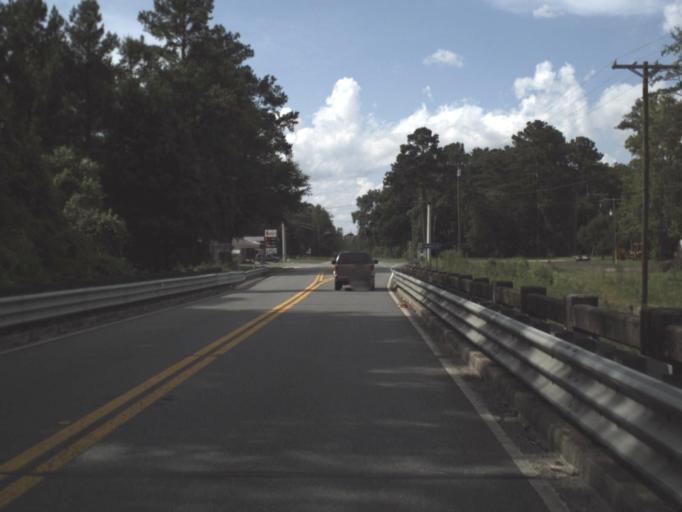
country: US
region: Florida
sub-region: Taylor County
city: Perry
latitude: 30.2863
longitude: -83.6315
